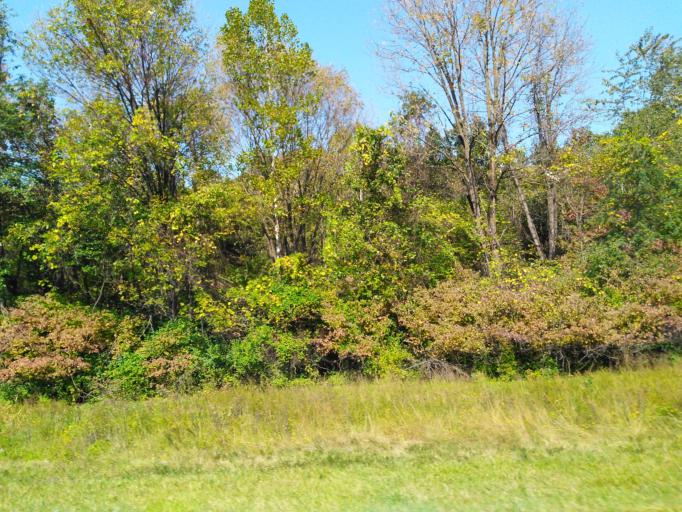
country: US
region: Missouri
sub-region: Saint Louis County
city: Valley Park
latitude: 38.5310
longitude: -90.5276
